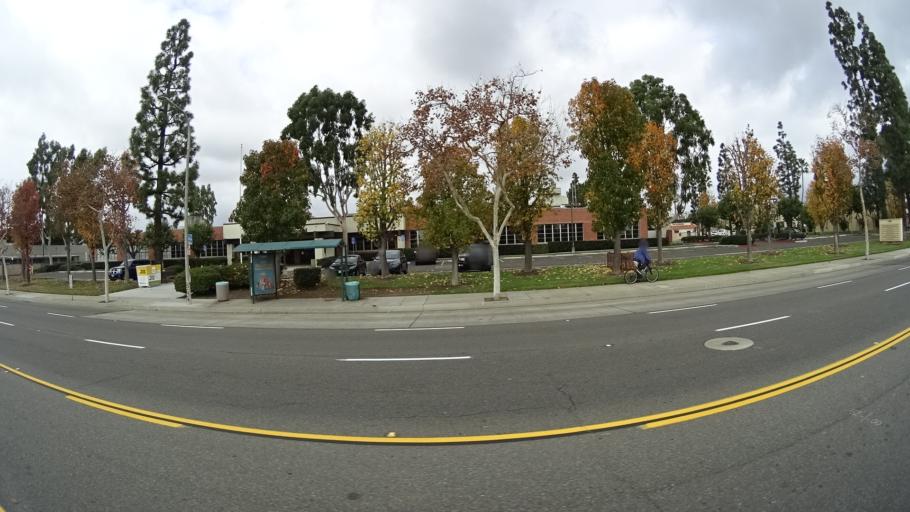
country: US
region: California
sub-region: Orange County
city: Santa Ana
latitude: 33.7600
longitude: -117.8925
